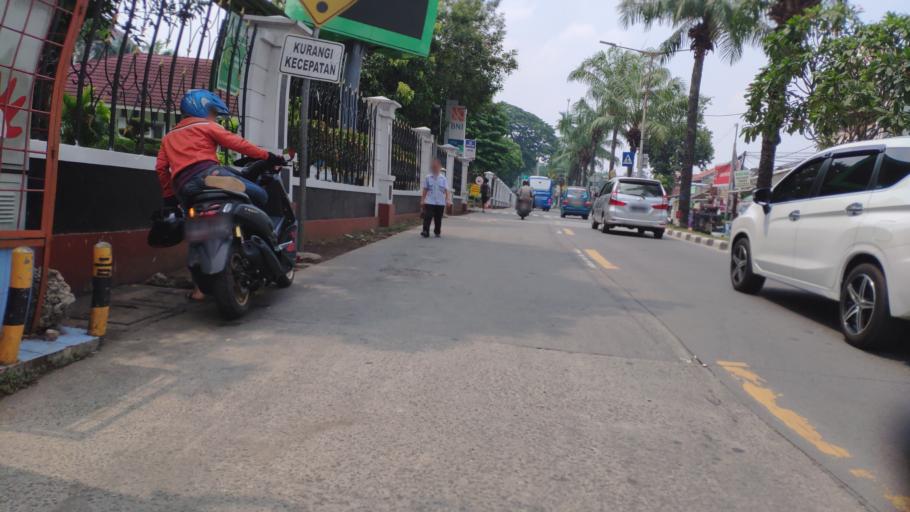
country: ID
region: West Java
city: Pamulang
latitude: -6.3042
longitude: 106.8210
